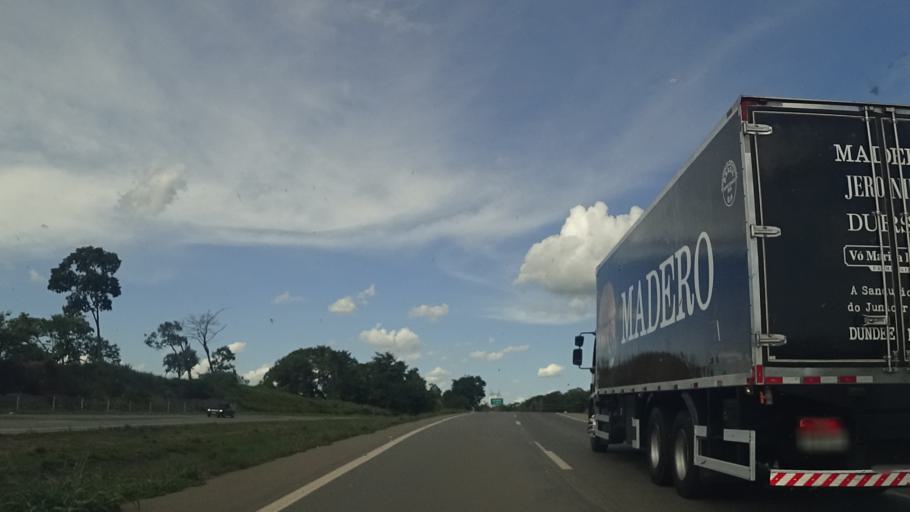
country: BR
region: Goias
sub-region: Piracanjuba
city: Piracanjuba
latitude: -17.2135
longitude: -49.2260
